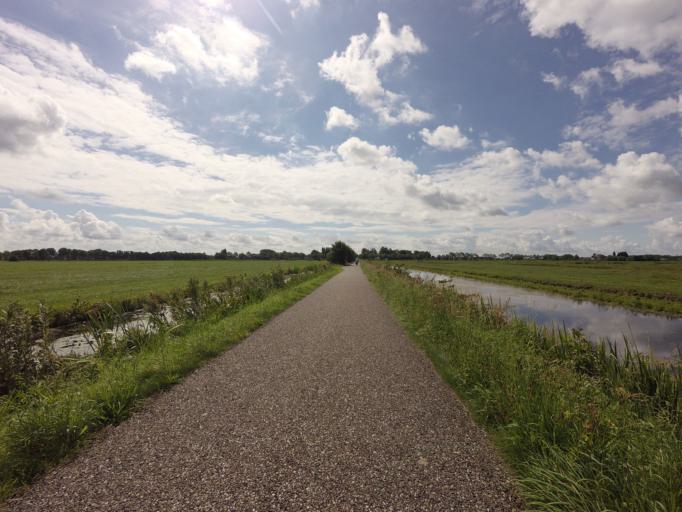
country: NL
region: South Holland
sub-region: Molenwaard
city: Liesveld
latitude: 51.9419
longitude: 4.8113
